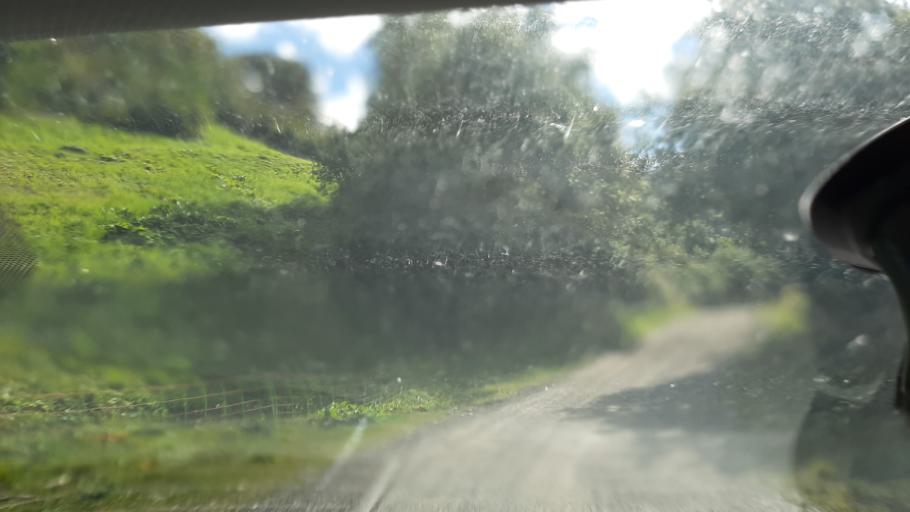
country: FR
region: Rhone-Alpes
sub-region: Departement de la Savoie
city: Saint-Michel-de-Maurienne
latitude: 45.1679
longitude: 6.4951
